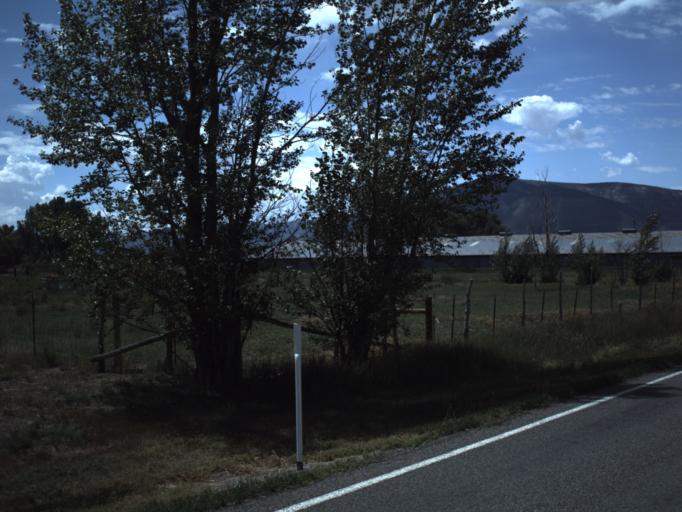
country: US
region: Utah
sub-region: Sanpete County
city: Moroni
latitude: 39.4760
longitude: -111.5695
